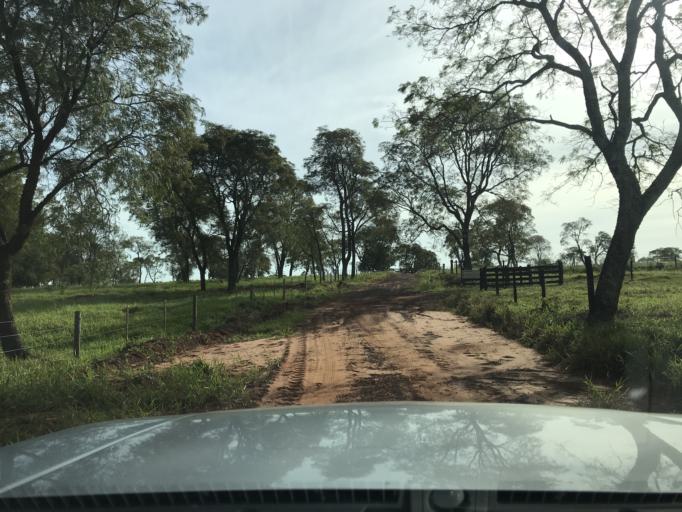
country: BR
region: Mato Grosso do Sul
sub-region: Iguatemi
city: Iguatemi
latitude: -23.6449
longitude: -54.5745
